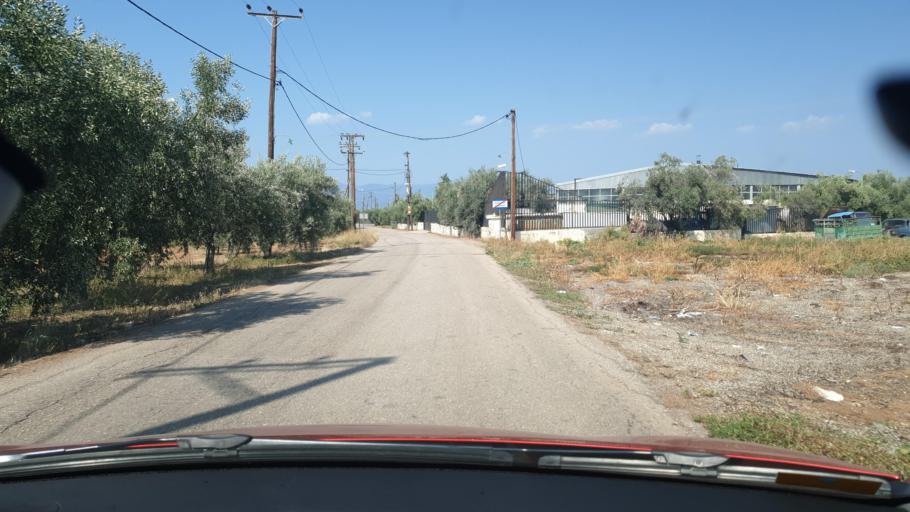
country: GR
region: Central Greece
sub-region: Nomos Fthiotidos
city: Livanates
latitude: 38.7206
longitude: 23.0508
